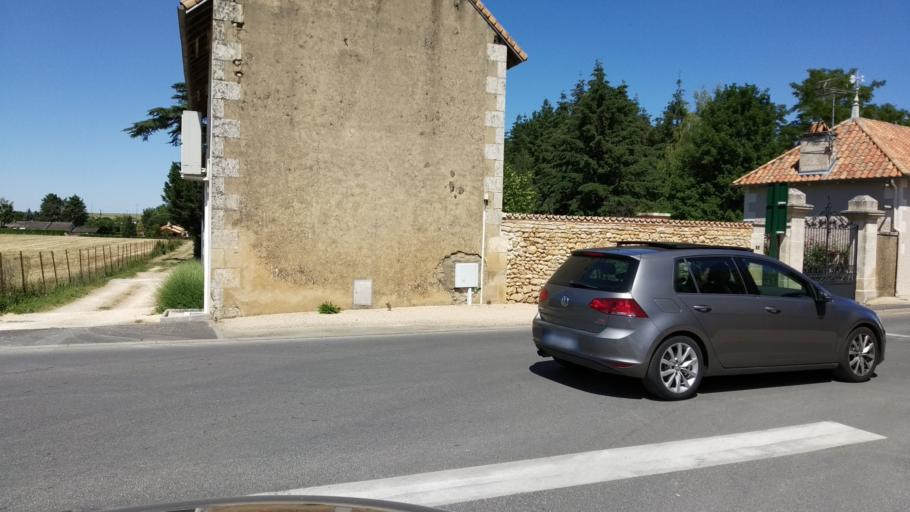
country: FR
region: Poitou-Charentes
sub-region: Departement de la Vienne
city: Biard
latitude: 46.6022
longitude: 0.2862
